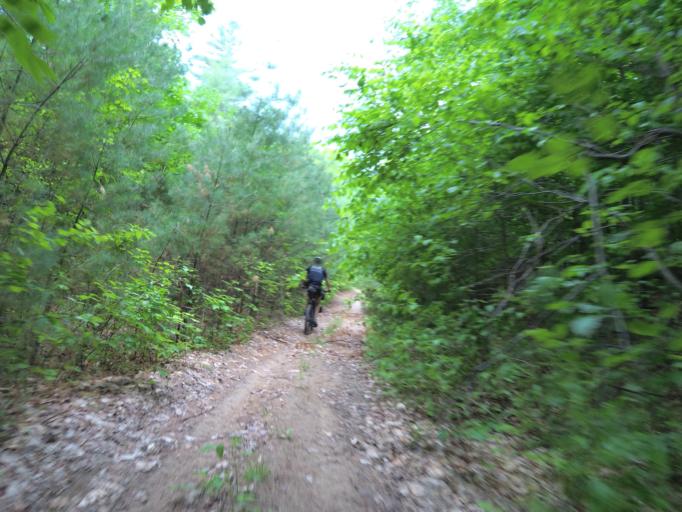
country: CA
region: Ontario
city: Renfrew
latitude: 45.0579
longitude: -76.8804
